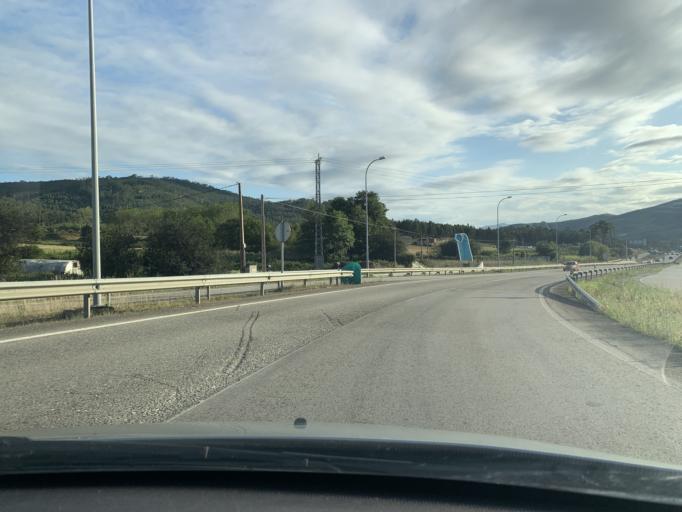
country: ES
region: Galicia
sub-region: Provincia de Lugo
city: Barreiros
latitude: 43.5398
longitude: -7.2521
